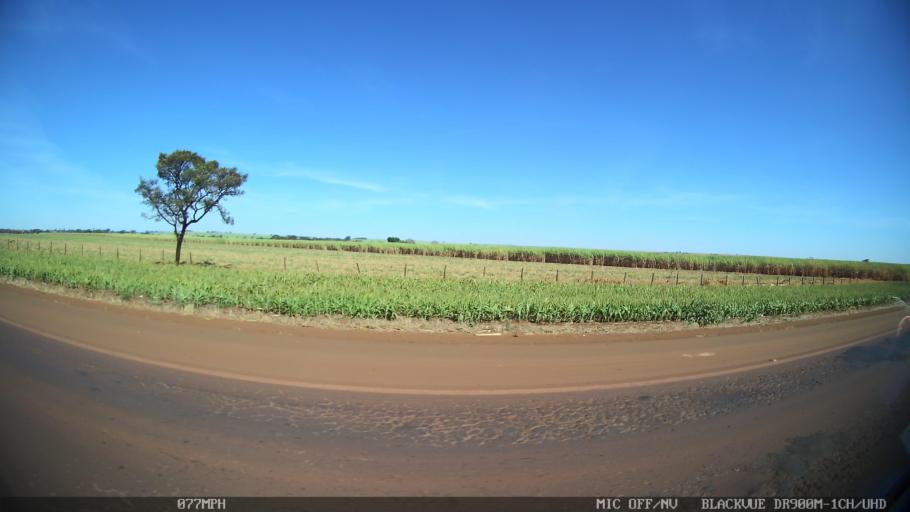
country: BR
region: Sao Paulo
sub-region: Ipua
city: Ipua
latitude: -20.5024
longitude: -47.9449
